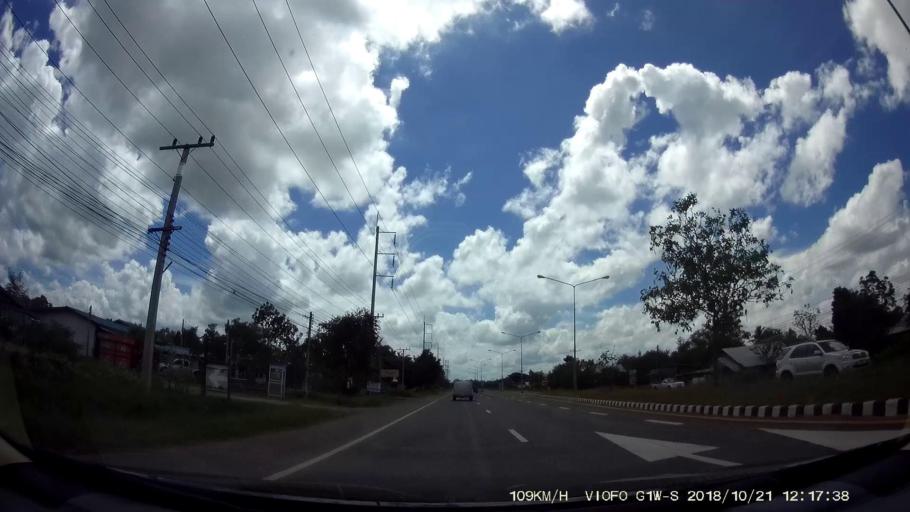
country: TH
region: Nakhon Ratchasima
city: Dan Khun Thot
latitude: 15.3290
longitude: 101.8194
